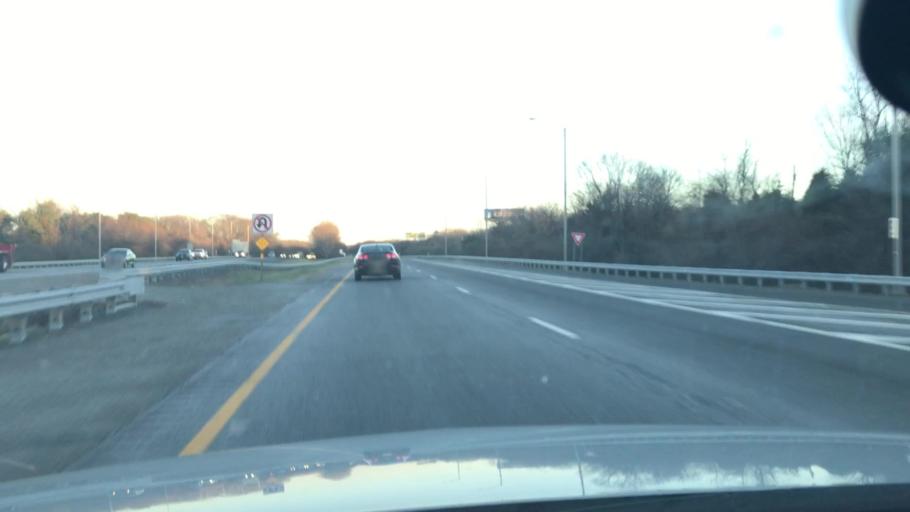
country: US
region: New Jersey
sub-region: Camden County
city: Sicklerville
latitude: 39.7314
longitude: -75.0069
